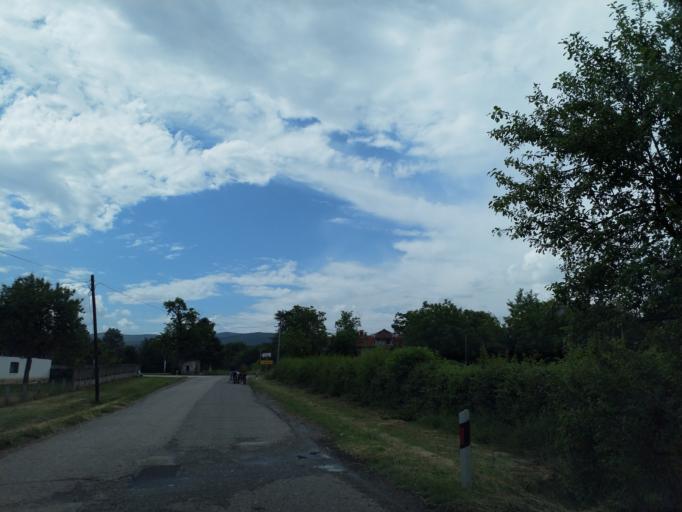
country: RS
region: Central Serbia
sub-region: Zajecarski Okrug
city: Boljevac
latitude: 43.8951
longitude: 21.9632
